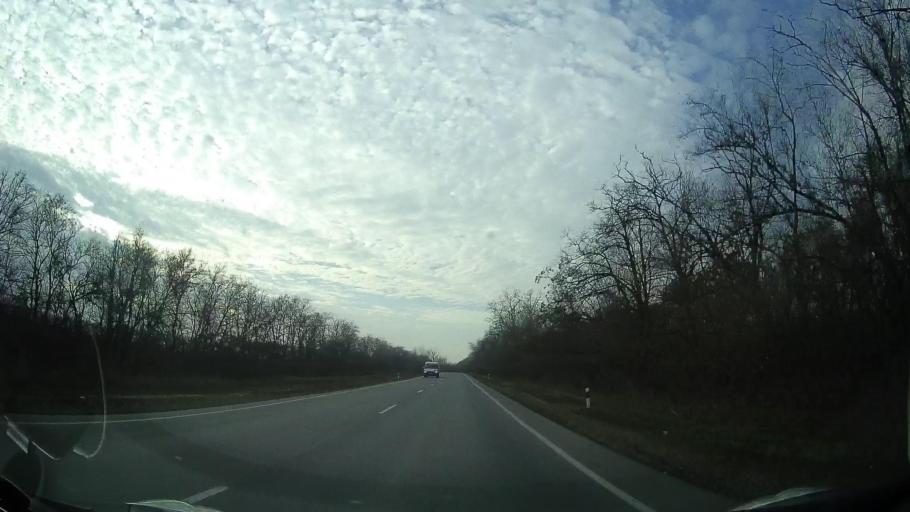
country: RU
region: Rostov
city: Bagayevskaya
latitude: 47.0960
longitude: 40.2872
